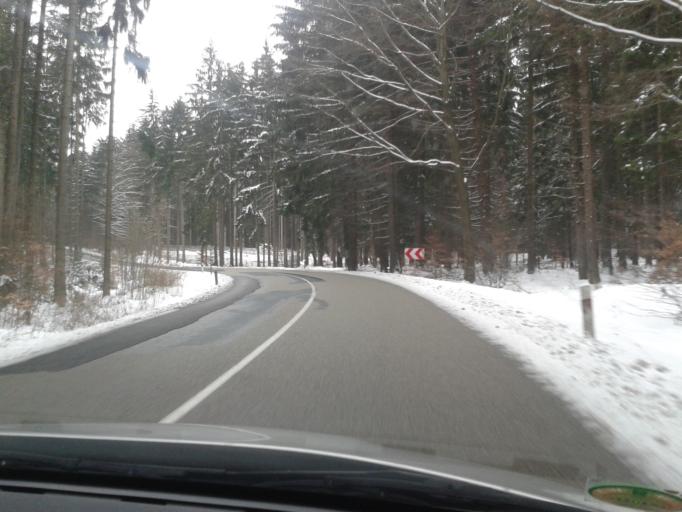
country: CZ
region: Olomoucky
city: Protivanov
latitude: 49.4740
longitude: 16.7882
